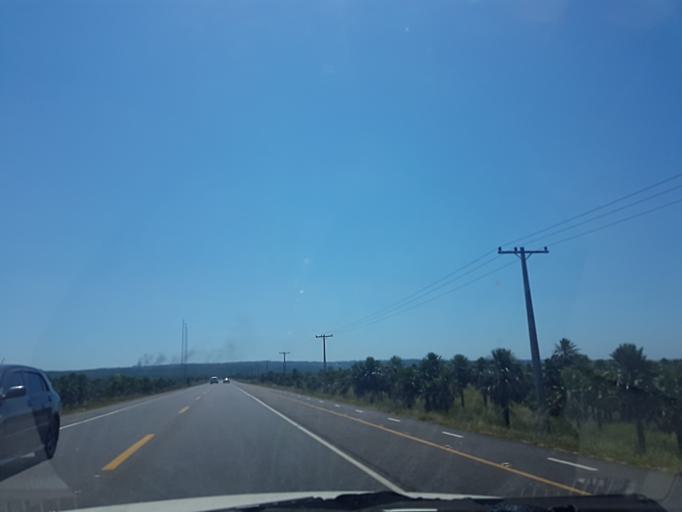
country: PY
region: Cordillera
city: Emboscada
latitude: -25.2078
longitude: -57.3805
